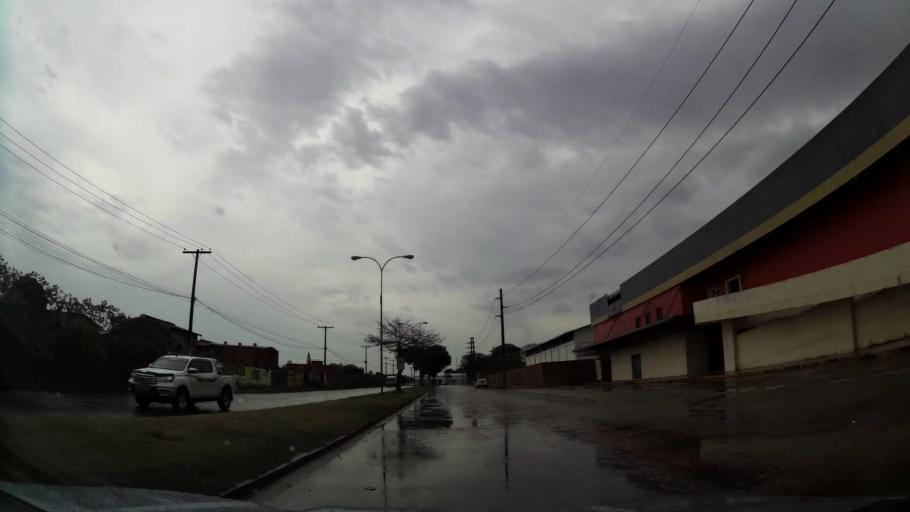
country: BO
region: Santa Cruz
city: Santa Cruz de la Sierra
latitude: -17.7909
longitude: -63.1545
